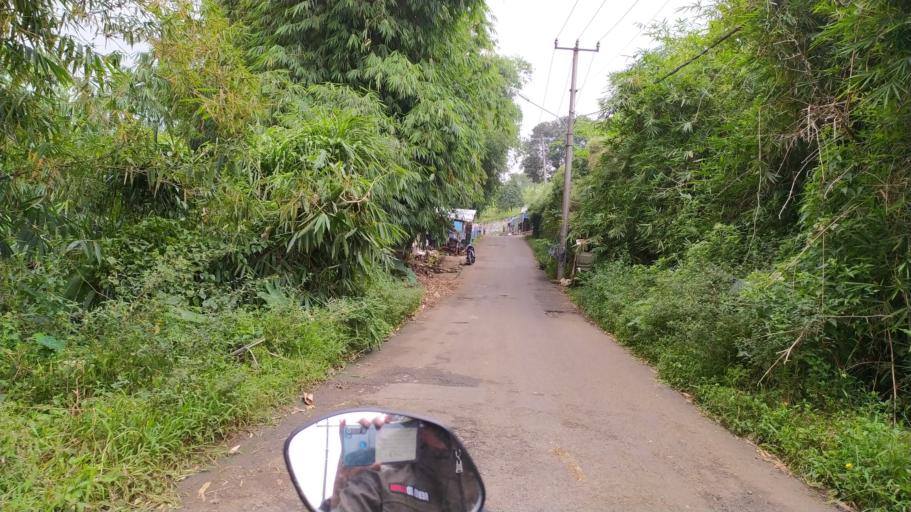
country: ID
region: West Java
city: Ciampea
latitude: -6.6431
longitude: 106.7047
